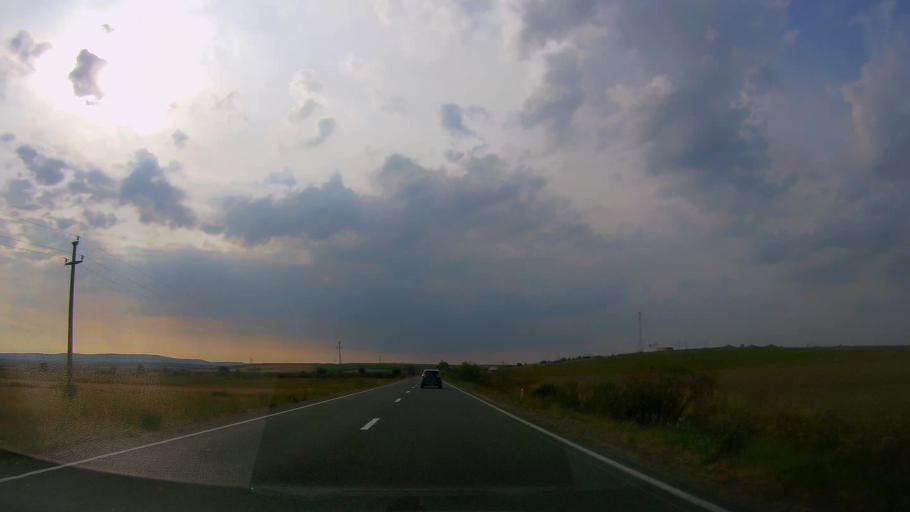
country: RO
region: Satu Mare
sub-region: Oras Ardud
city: Ardud
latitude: 47.6164
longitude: 22.8754
